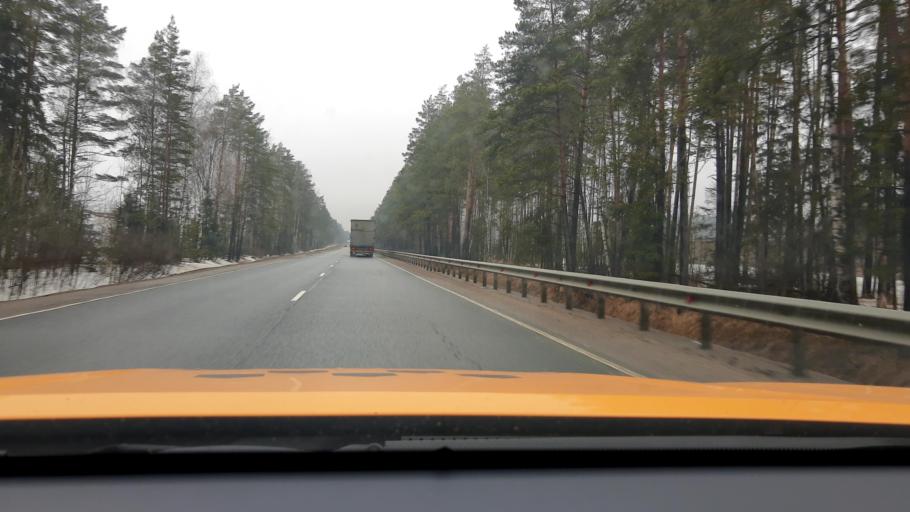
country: RU
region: Moskovskaya
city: Krasnoarmeysk
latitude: 56.0220
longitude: 38.2364
